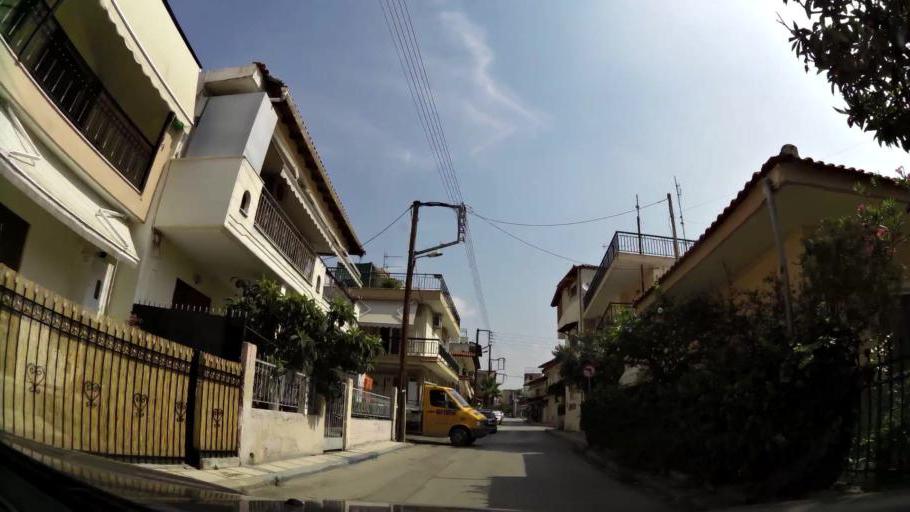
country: GR
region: Central Macedonia
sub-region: Nomos Thessalonikis
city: Stavroupoli
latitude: 40.6711
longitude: 22.9354
